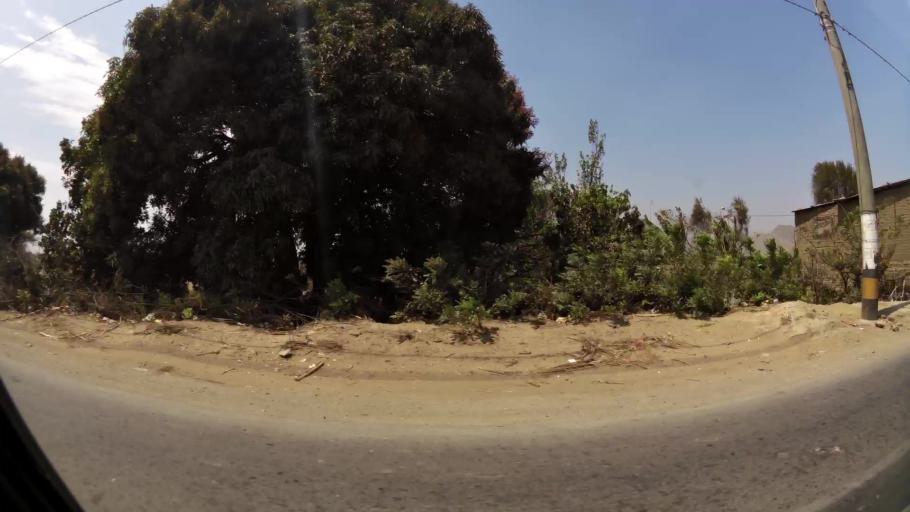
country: PE
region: La Libertad
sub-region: Chepen
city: Chepen
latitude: -7.1983
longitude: -79.4286
